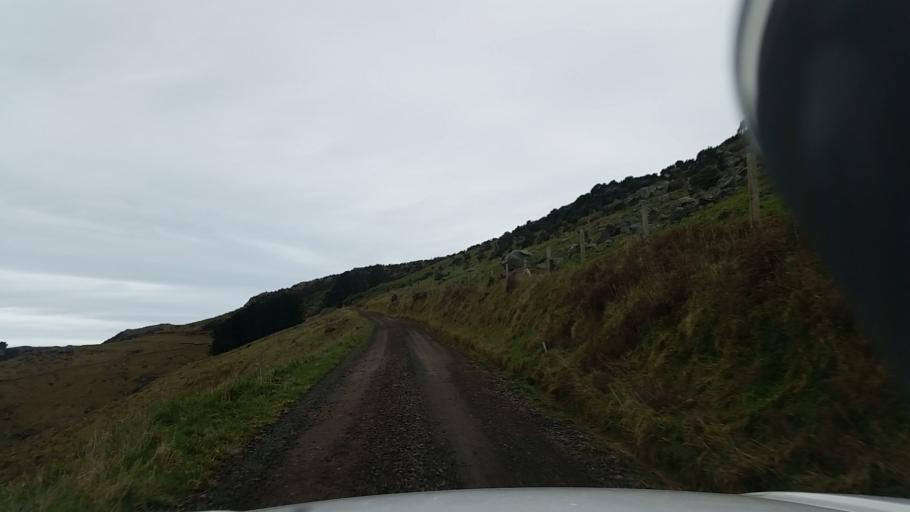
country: NZ
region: Canterbury
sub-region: Christchurch City
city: Christchurch
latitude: -43.7454
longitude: 173.0071
